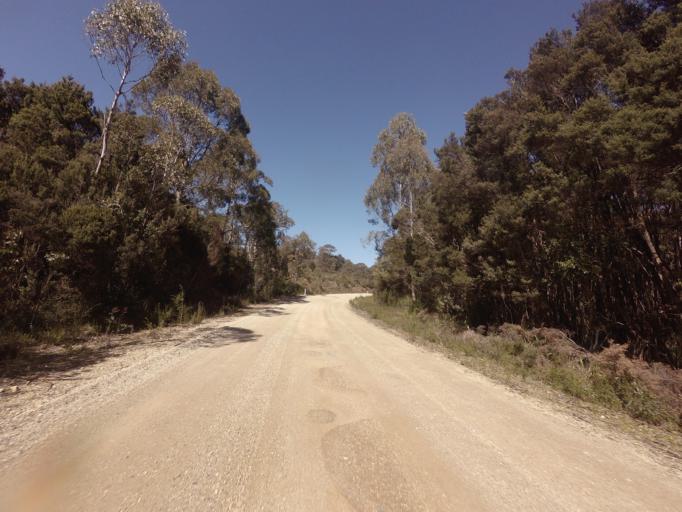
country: AU
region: Tasmania
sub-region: Huon Valley
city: Geeveston
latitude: -42.9057
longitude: 146.3694
